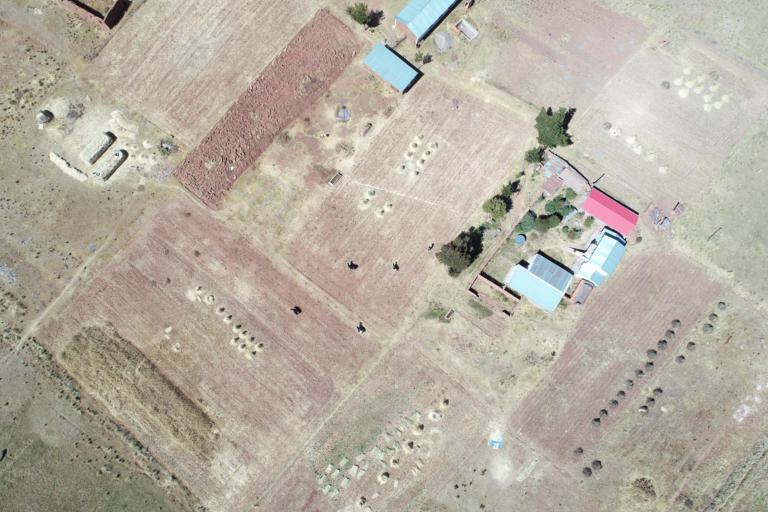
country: BO
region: La Paz
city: Tiahuanaco
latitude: -16.6005
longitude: -68.7760
